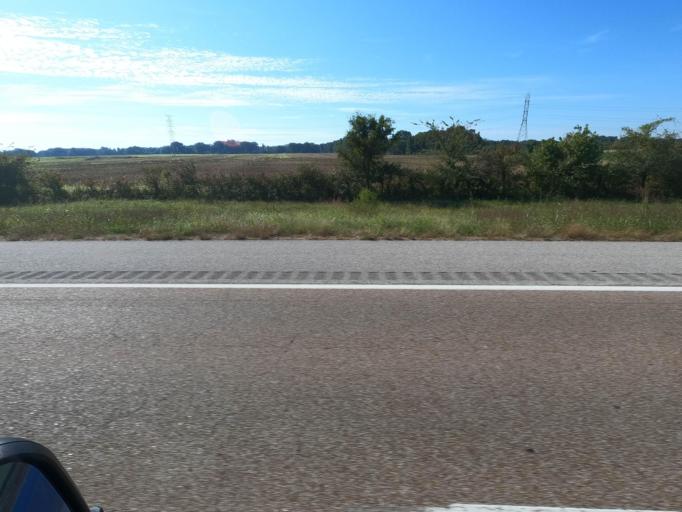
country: US
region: Tennessee
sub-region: Shelby County
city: Millington
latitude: 35.3105
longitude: -89.8557
